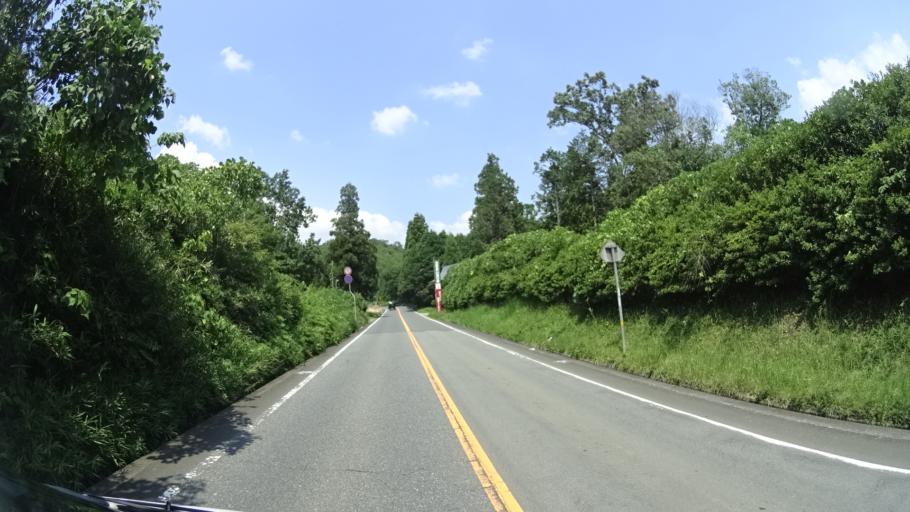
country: JP
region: Kyoto
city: Fukuchiyama
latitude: 35.2602
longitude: 135.1464
